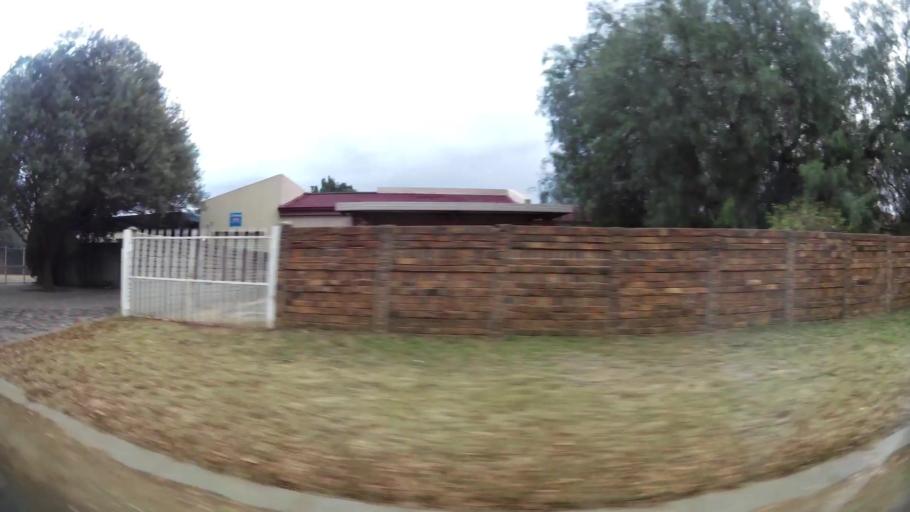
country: ZA
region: Orange Free State
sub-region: Lejweleputswa District Municipality
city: Welkom
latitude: -27.9512
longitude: 26.7342
